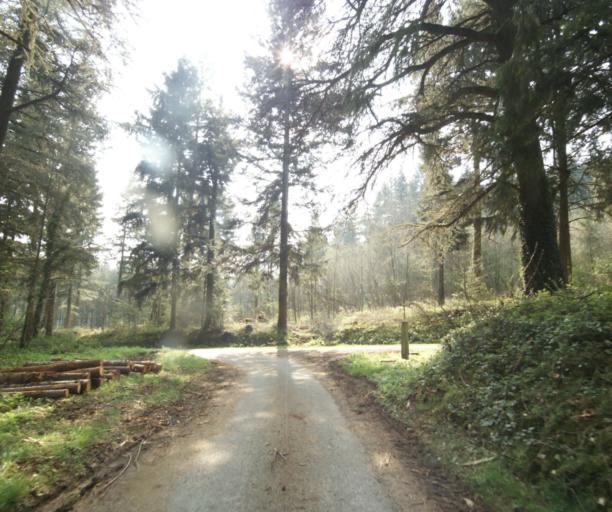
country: FR
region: Bourgogne
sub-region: Departement de Saone-et-Loire
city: Charolles
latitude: 46.4908
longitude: 4.4299
